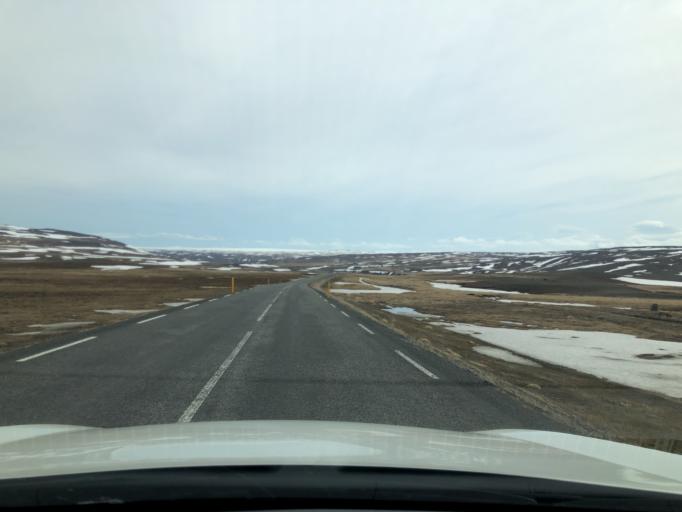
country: IS
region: East
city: Egilsstadir
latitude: 65.3048
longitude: -15.3130
